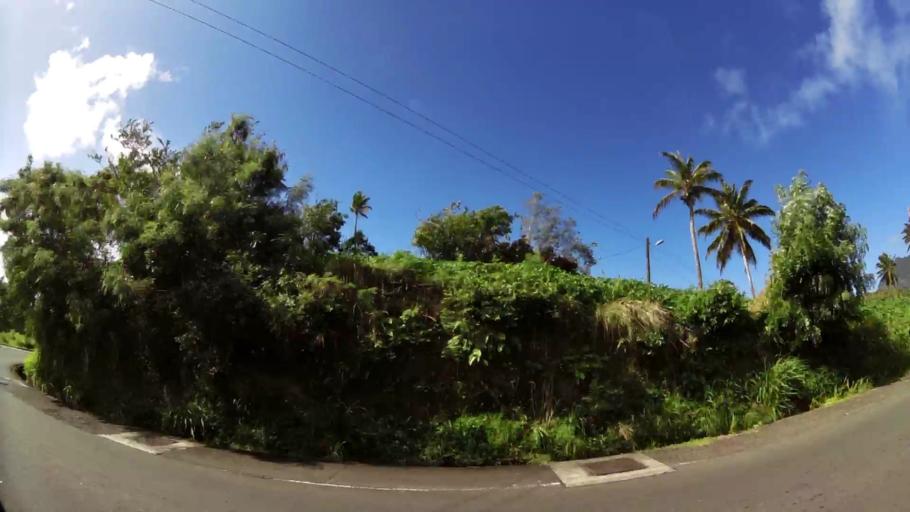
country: LC
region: Choiseul Quarter
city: Choiseul
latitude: 13.7974
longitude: -61.0380
